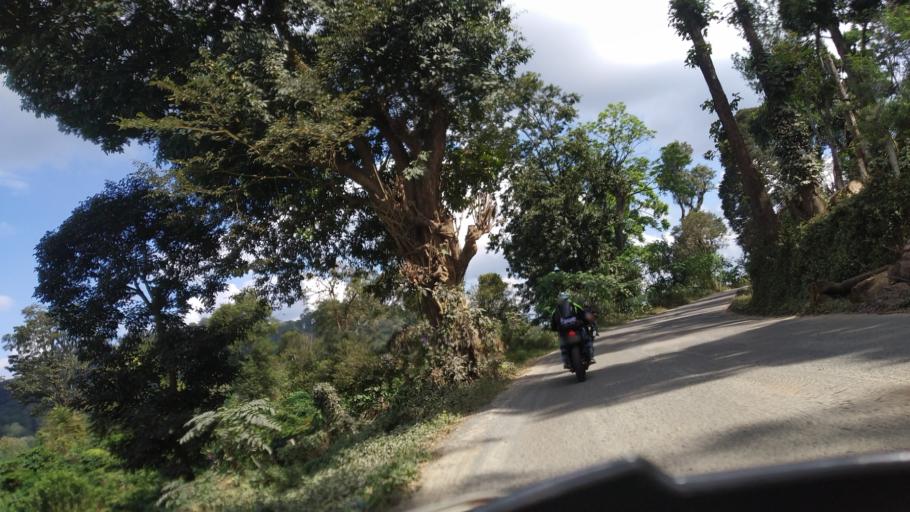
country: IN
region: Karnataka
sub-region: Kodagu
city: Ponnampet
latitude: 11.9633
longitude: 76.0582
